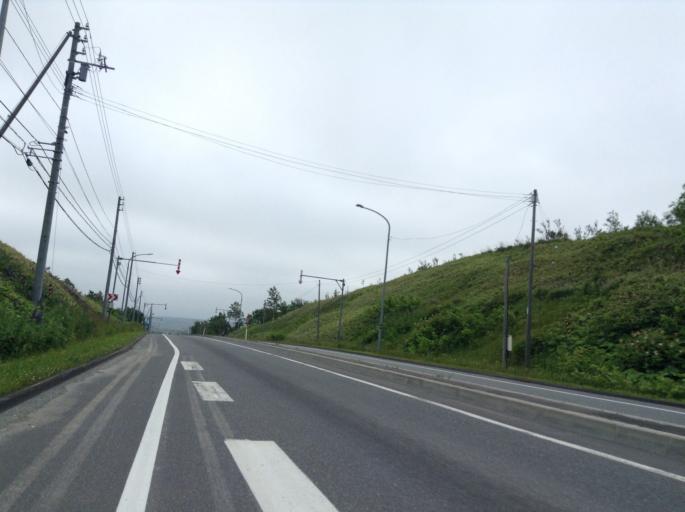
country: JP
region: Hokkaido
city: Wakkanai
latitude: 45.3737
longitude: 141.7165
